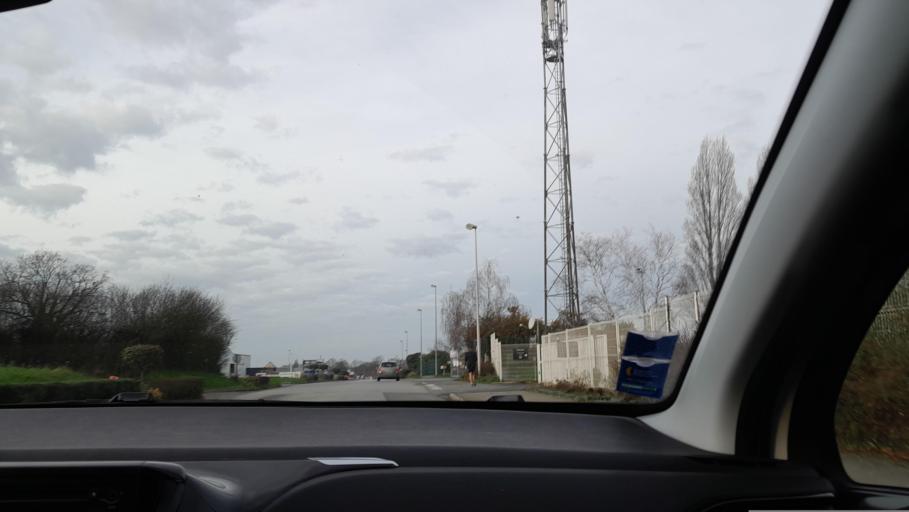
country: FR
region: Brittany
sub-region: Departement d'Ille-et-Vilaine
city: La Guerche-de-Bretagne
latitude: 47.9338
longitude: -1.2255
